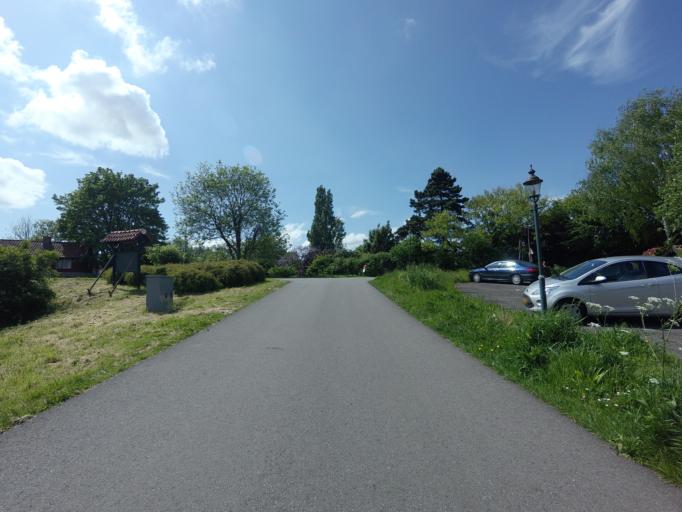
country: NL
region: South Holland
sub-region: Gemeente Zwijndrecht
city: Heerjansdam
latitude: 51.8528
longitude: 4.5659
